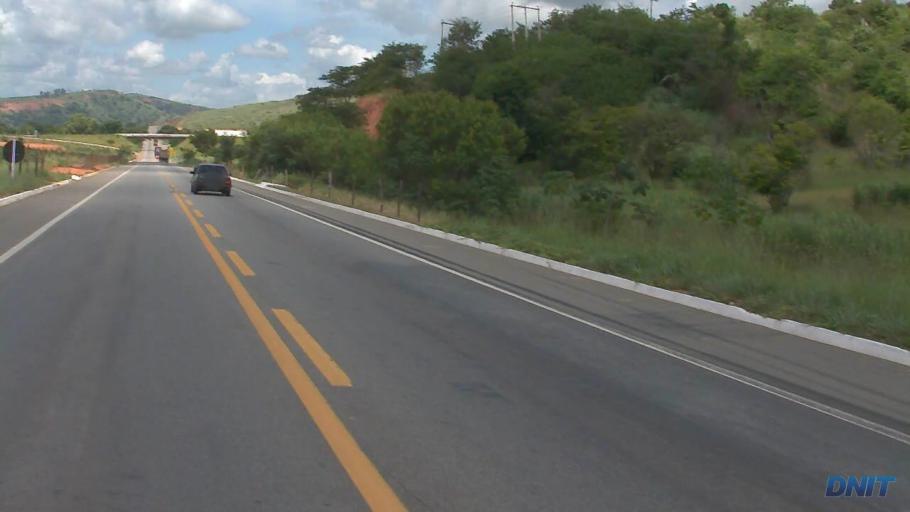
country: BR
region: Minas Gerais
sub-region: Governador Valadares
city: Governador Valadares
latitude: -18.9235
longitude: -42.0229
